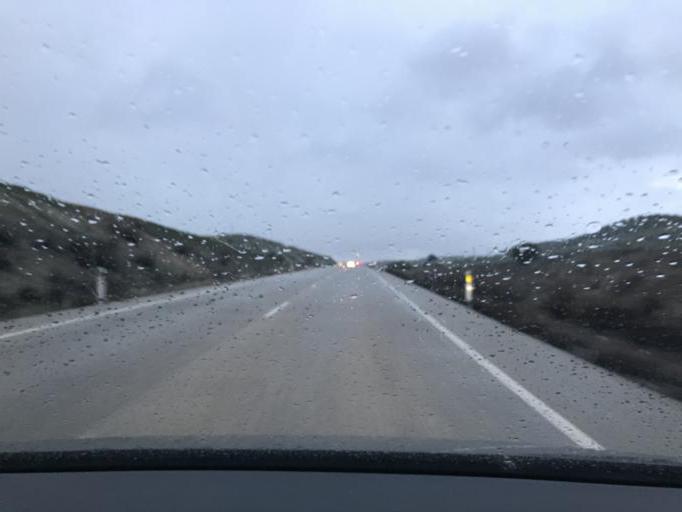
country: ES
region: Andalusia
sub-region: Provincia de Granada
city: Campotejar
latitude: 37.4689
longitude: -3.5856
